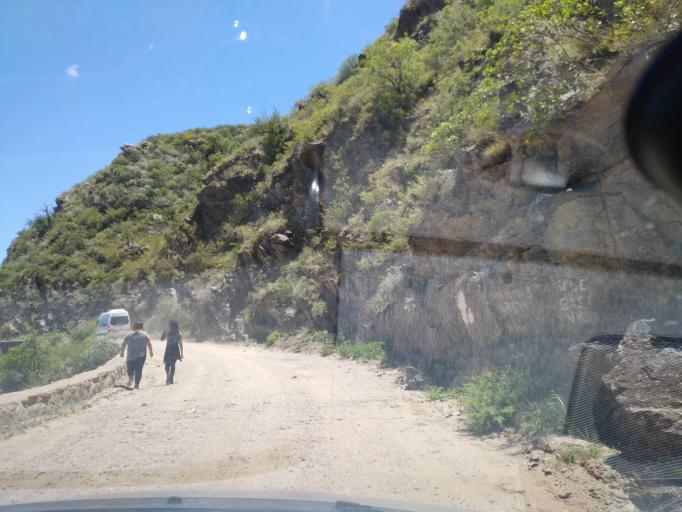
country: AR
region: Cordoba
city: Salsacate
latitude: -31.3770
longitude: -65.4072
